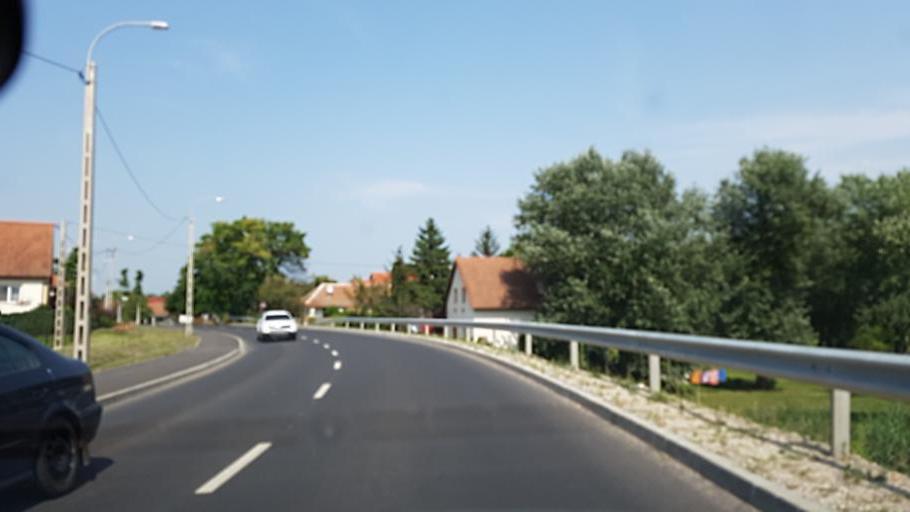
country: HU
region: Heves
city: Poroszlo
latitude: 47.6481
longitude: 20.6652
